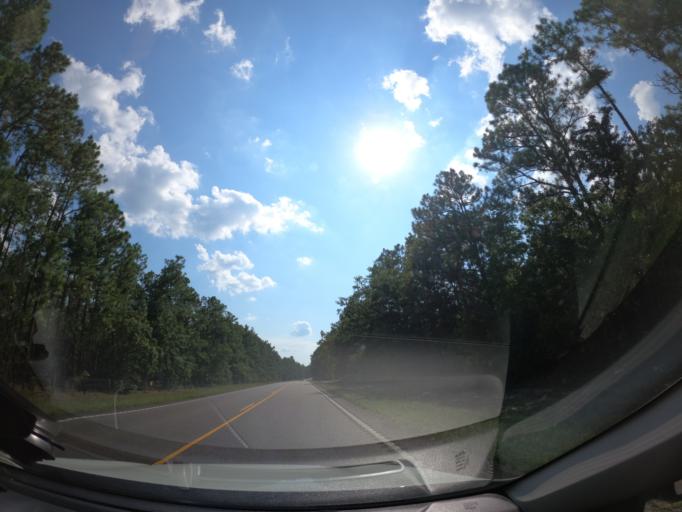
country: US
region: South Carolina
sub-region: Aiken County
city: New Ellenton
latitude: 33.3928
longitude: -81.5632
